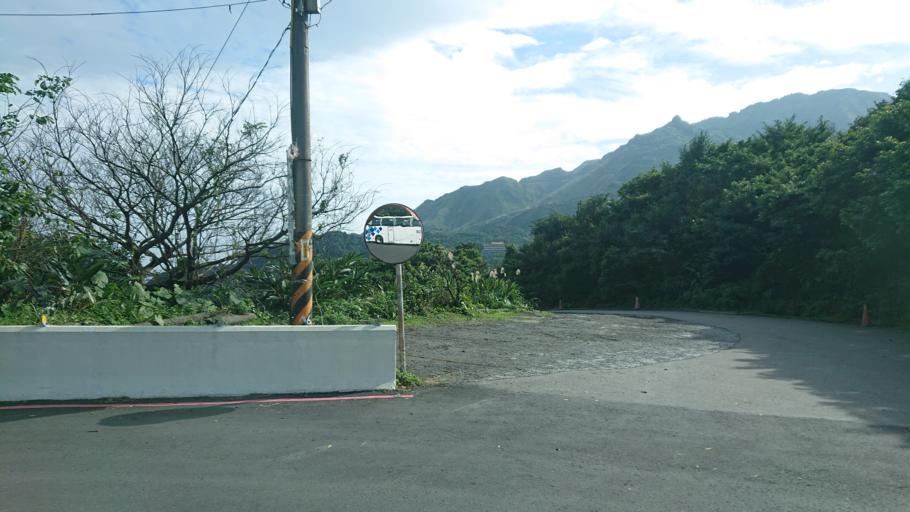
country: TW
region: Taiwan
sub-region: Keelung
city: Keelung
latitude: 25.1111
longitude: 121.8499
